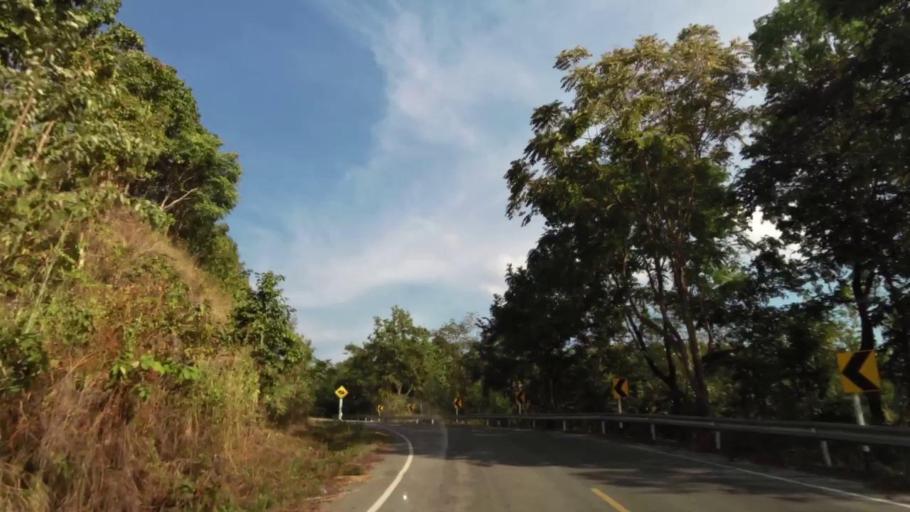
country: TH
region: Chiang Rai
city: Khun Tan
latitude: 19.8802
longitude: 100.3065
